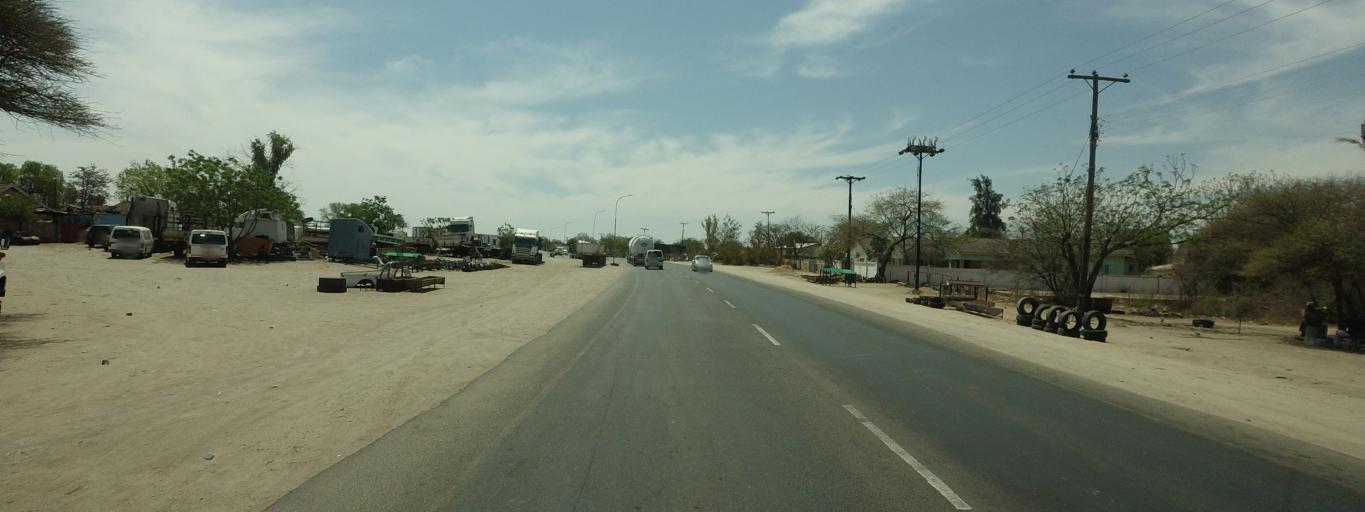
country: BW
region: North East
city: Francistown
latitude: -21.1654
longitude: 27.4942
